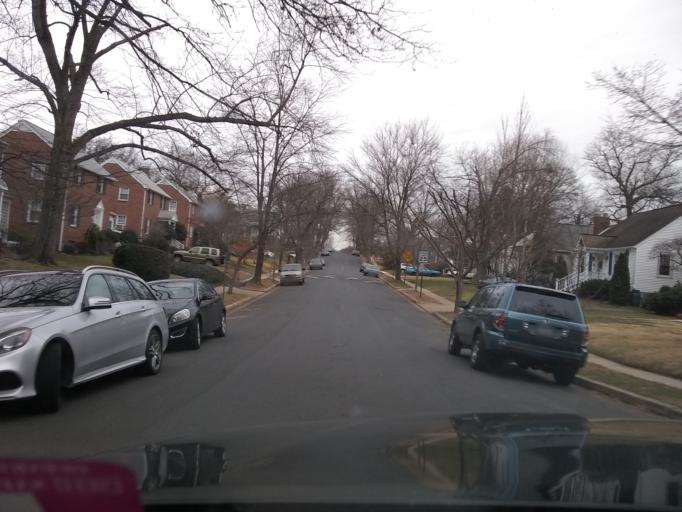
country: US
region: Virginia
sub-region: Arlington County
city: Arlington
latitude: 38.8896
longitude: -77.1260
